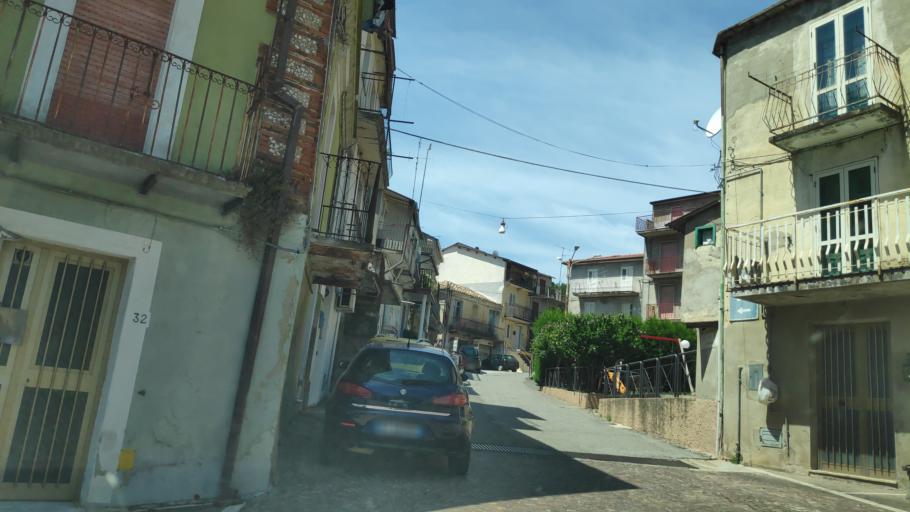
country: IT
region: Calabria
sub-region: Provincia di Catanzaro
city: Palermiti
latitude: 38.7509
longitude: 16.4532
